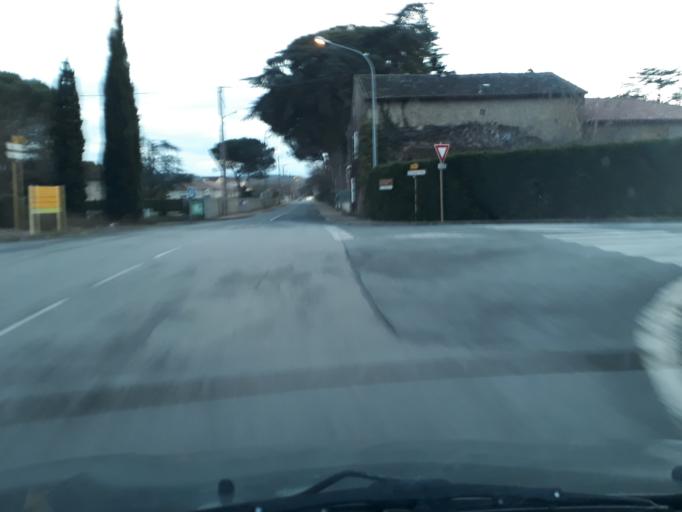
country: FR
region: Midi-Pyrenees
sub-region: Departement de la Haute-Garonne
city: Carbonne
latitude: 43.3046
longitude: 1.2296
